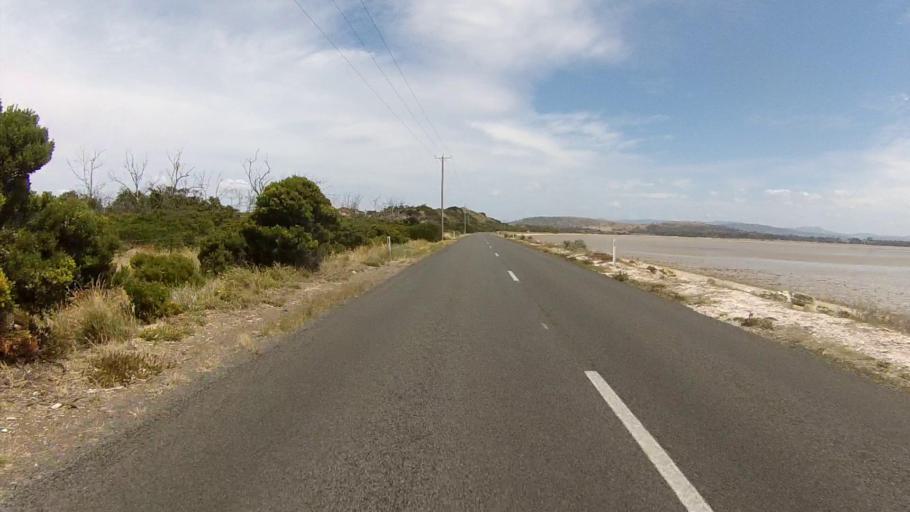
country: AU
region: Tasmania
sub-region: Clarence
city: Sandford
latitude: -43.0299
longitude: 147.4631
